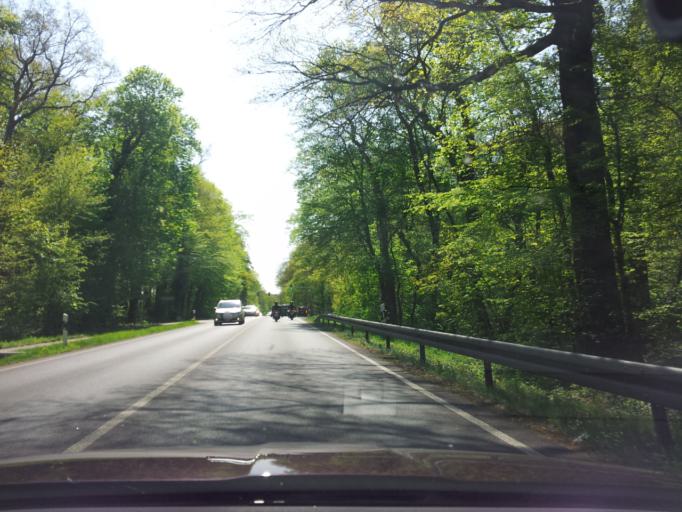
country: DE
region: Brandenburg
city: Michendorf
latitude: 52.2797
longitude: 13.0086
